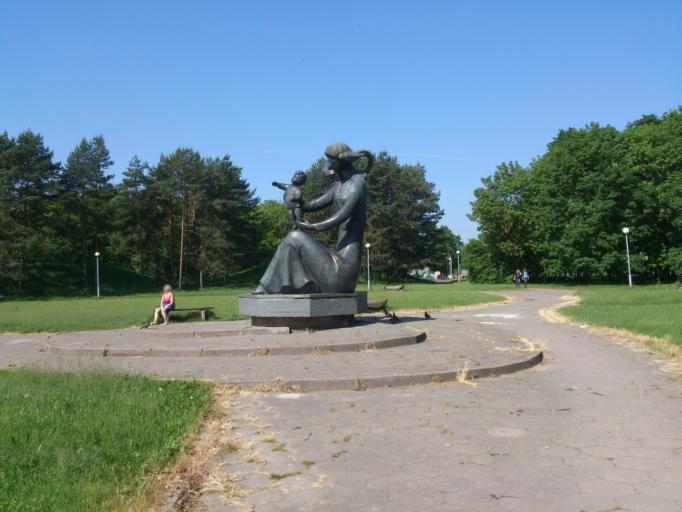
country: LT
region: Kauno apskritis
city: Dainava (Kaunas)
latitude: 54.9151
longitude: 23.9706
